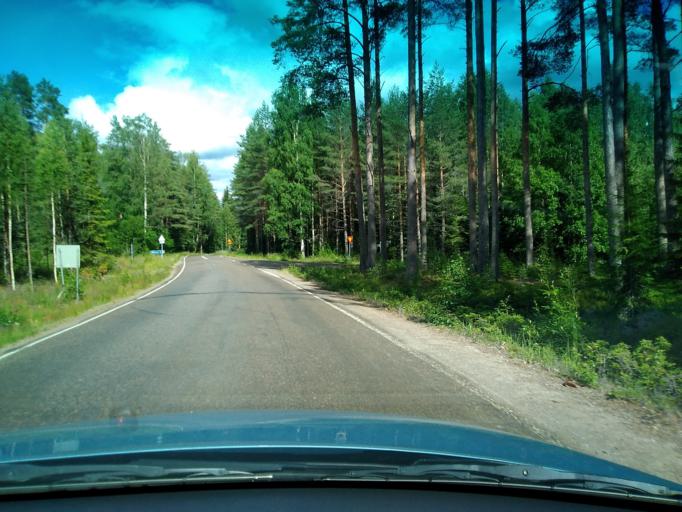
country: FI
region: Central Finland
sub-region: Saarijaervi-Viitasaari
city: Saarijaervi
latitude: 62.7334
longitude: 25.1211
